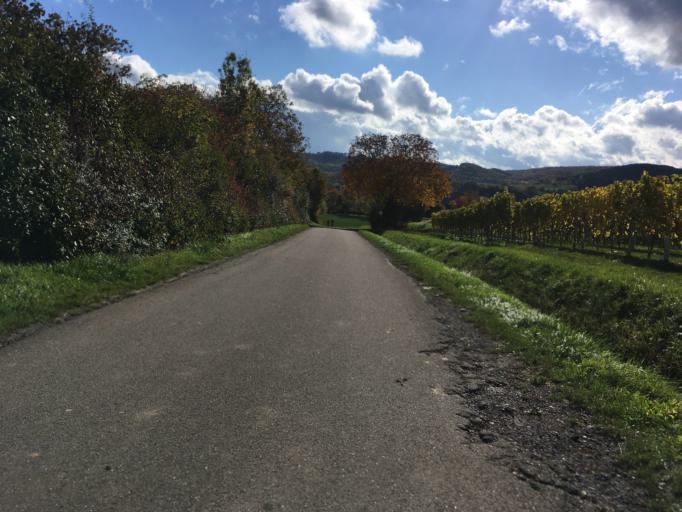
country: DE
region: Baden-Wuerttemberg
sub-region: Regierungsbezirk Stuttgart
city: Pfedelbach
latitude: 49.1865
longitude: 9.4804
